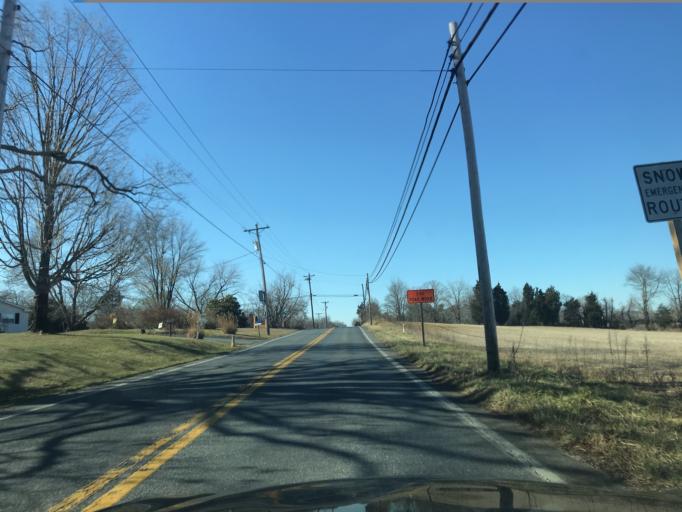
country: US
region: Maryland
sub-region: Charles County
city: Saint Charles
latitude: 38.5854
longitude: -76.9578
